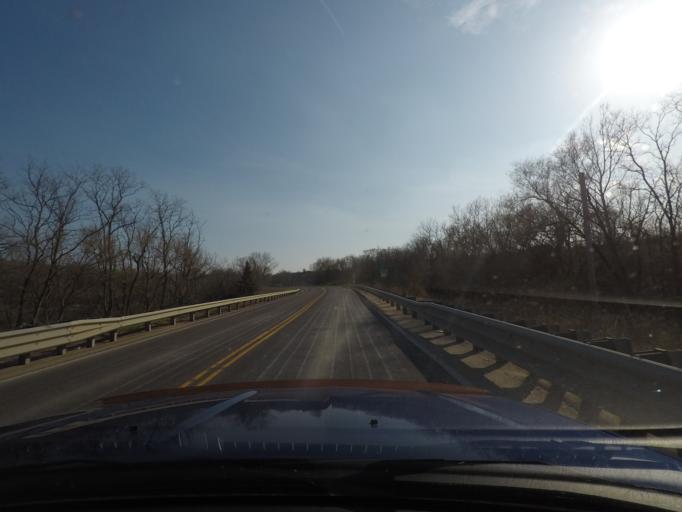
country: US
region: Kansas
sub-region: Douglas County
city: Lawrence
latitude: 39.0474
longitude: -95.3889
